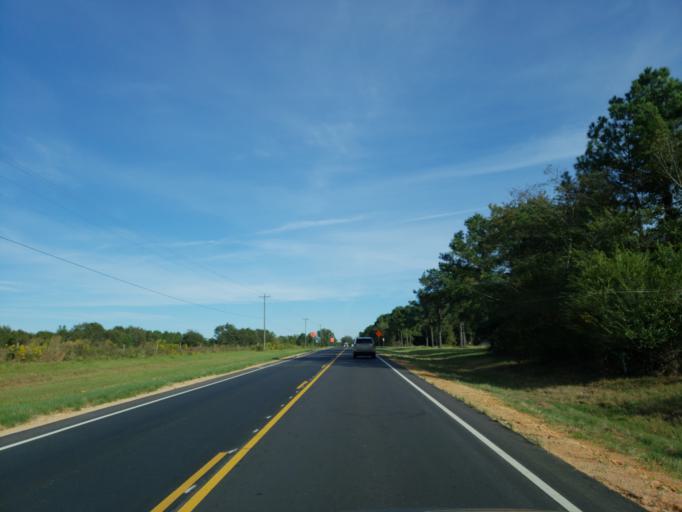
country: US
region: Georgia
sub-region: Houston County
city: Perry
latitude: 32.4864
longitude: -83.8128
